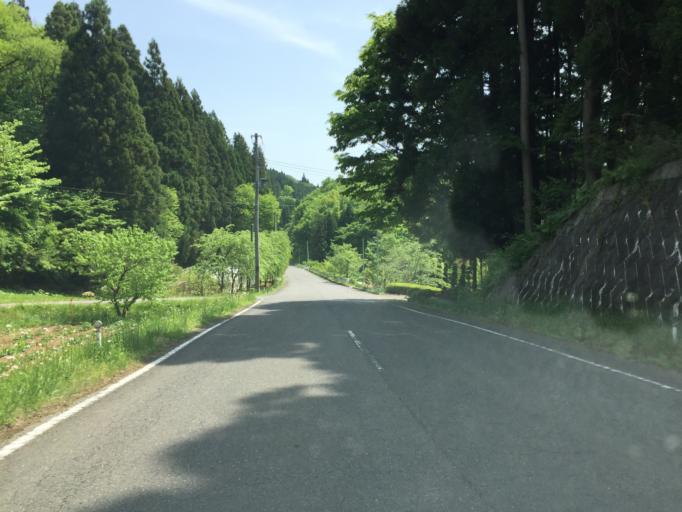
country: JP
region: Fukushima
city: Ishikawa
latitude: 37.1712
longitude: 140.5058
